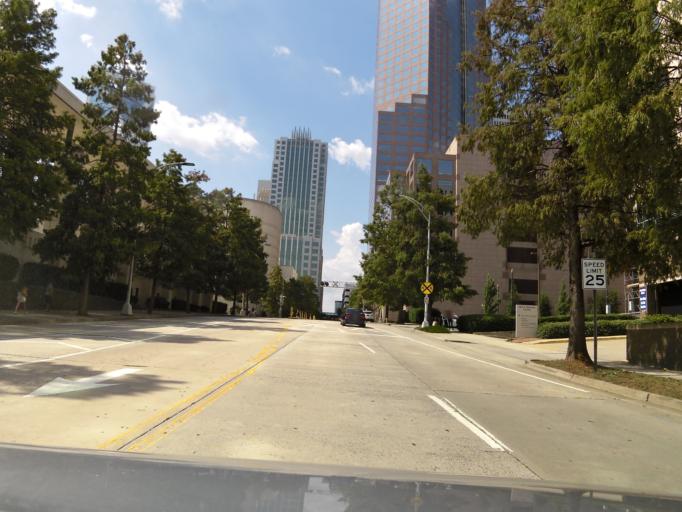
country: US
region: North Carolina
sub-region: Mecklenburg County
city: Charlotte
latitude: 35.2224
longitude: -80.8435
